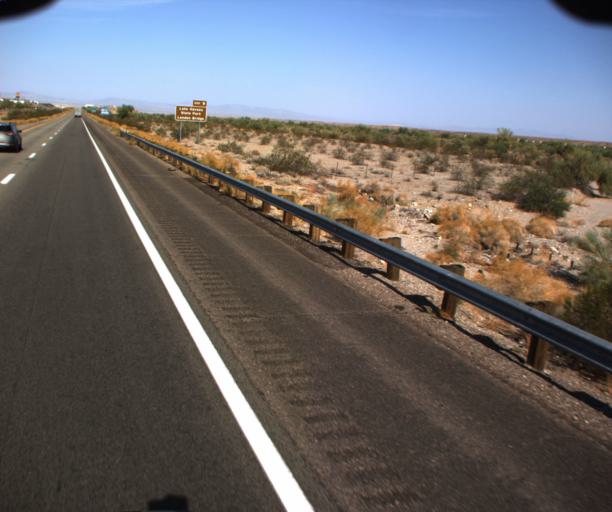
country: US
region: Arizona
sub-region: Mohave County
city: Desert Hills
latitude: 34.7302
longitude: -114.3010
